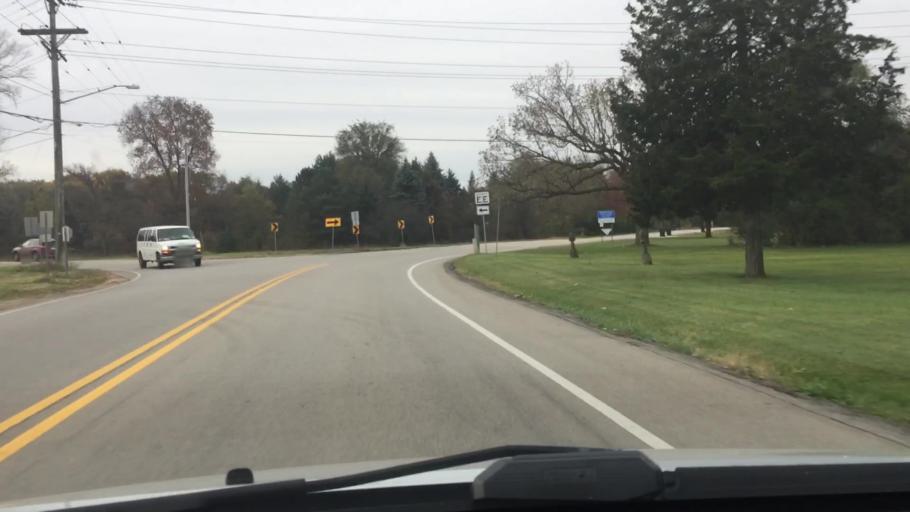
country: US
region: Wisconsin
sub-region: Waukesha County
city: North Prairie
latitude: 42.9082
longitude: -88.4084
